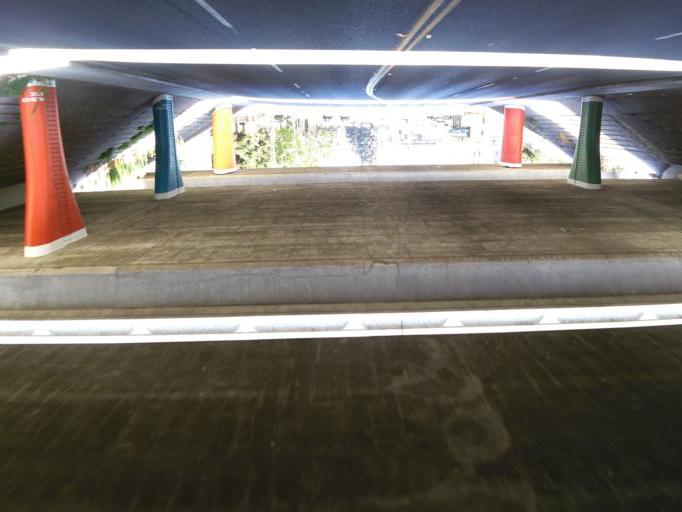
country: US
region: California
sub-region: Santa Clara County
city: Buena Vista
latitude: 37.3160
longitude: -121.9068
